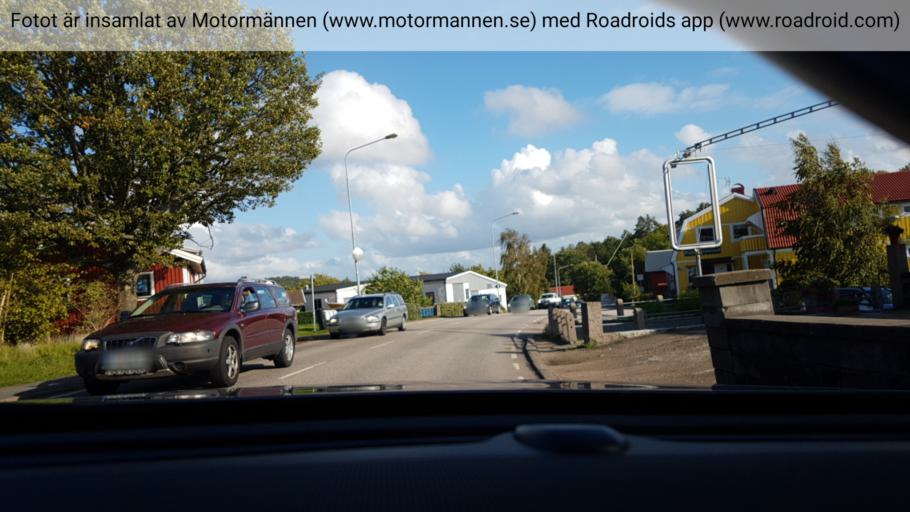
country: SE
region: Vaestra Goetaland
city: Svanesund
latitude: 58.1427
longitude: 11.8231
